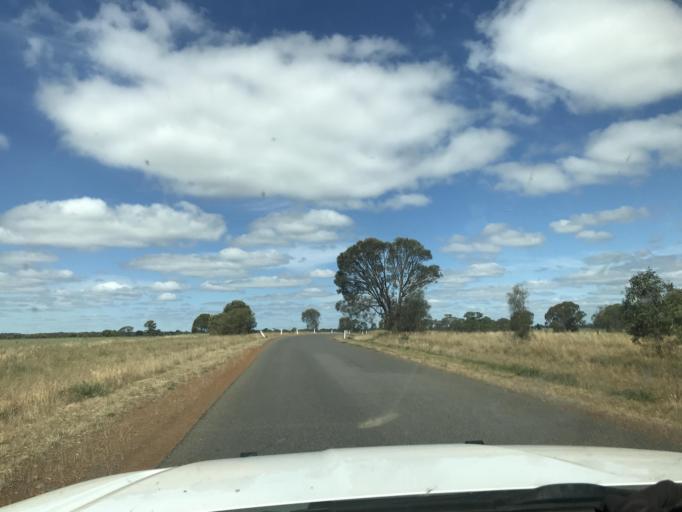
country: AU
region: South Australia
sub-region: Naracoorte and Lucindale
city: Naracoorte
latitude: -36.9922
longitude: 141.2883
